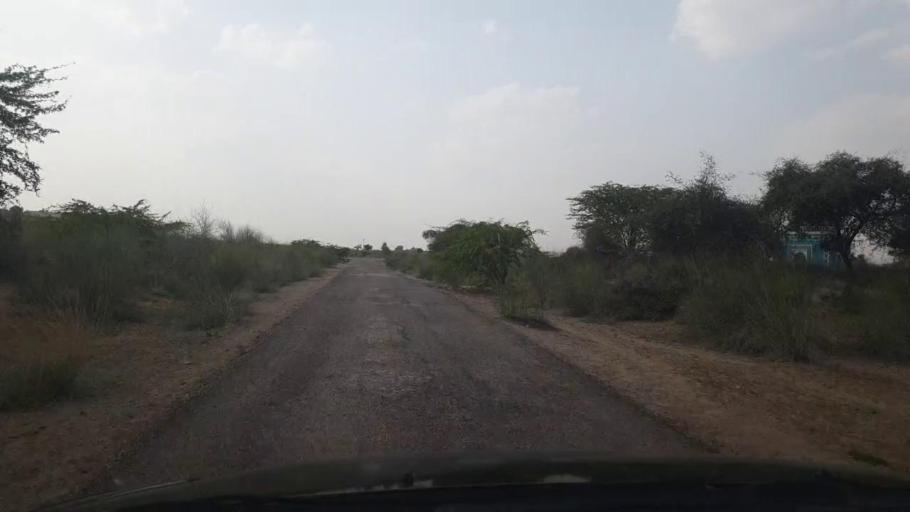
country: PK
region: Sindh
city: Islamkot
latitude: 24.9891
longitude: 70.5714
